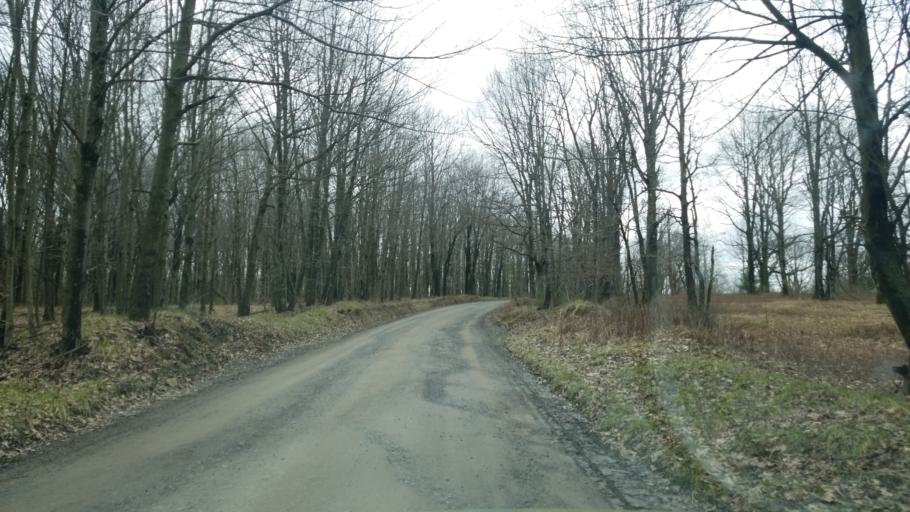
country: US
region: Pennsylvania
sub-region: Clearfield County
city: Shiloh
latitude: 41.1810
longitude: -78.3372
